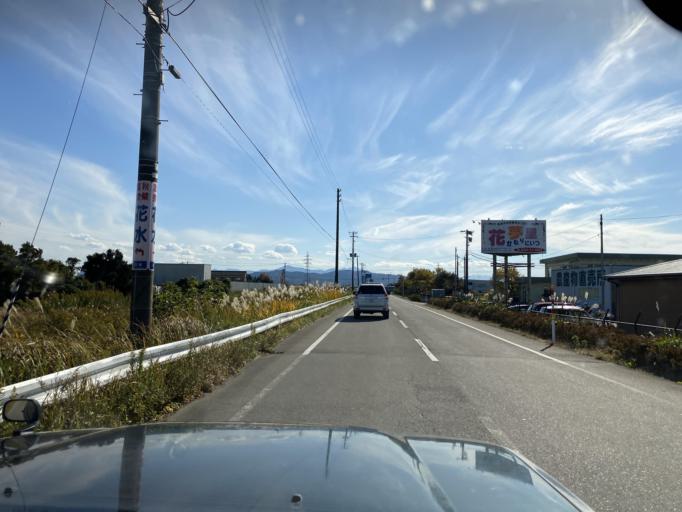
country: JP
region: Niigata
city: Niitsu-honcho
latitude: 37.7929
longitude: 139.0794
